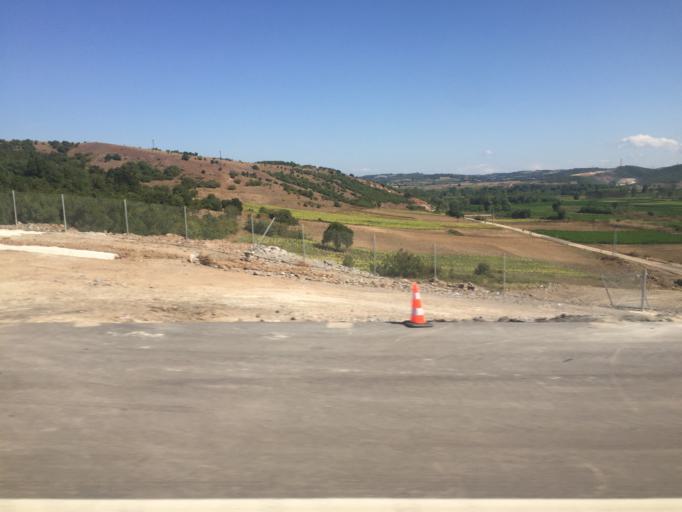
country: TR
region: Bursa
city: Mahmudiye
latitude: 40.2652
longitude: 28.6511
